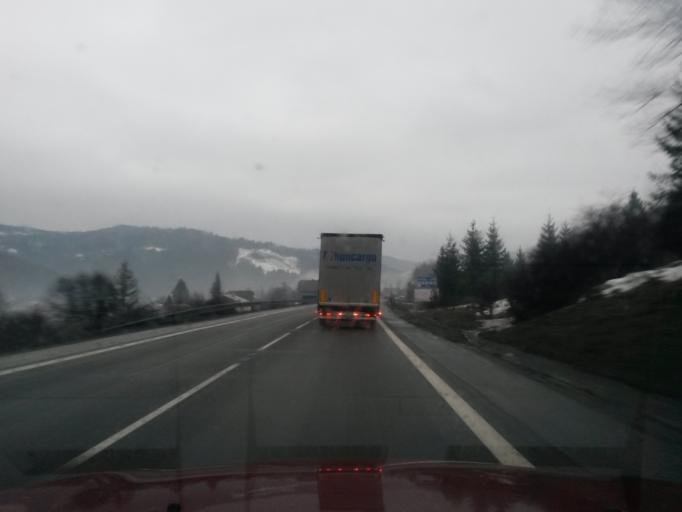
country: SK
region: Zilinsky
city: Cadca
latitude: 49.3892
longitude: 18.8379
